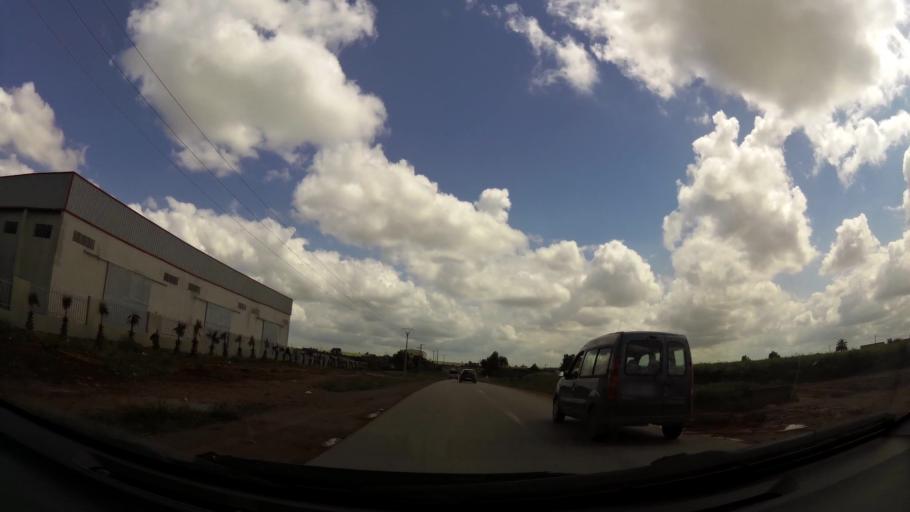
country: MA
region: Chaouia-Ouardigha
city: Nouaseur
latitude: 33.3314
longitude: -7.7345
